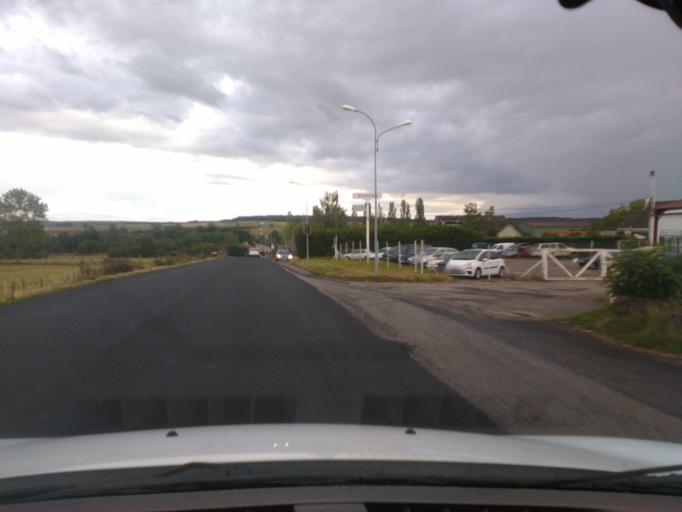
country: FR
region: Lorraine
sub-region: Departement de Meurthe-et-Moselle
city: Vezelise
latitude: 48.4002
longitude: 6.1355
